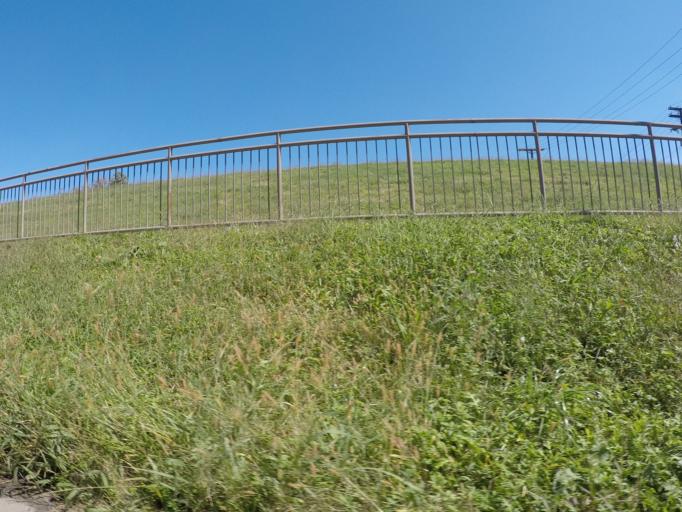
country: US
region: West Virginia
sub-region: Cabell County
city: Huntington
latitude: 38.4179
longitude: -82.3893
